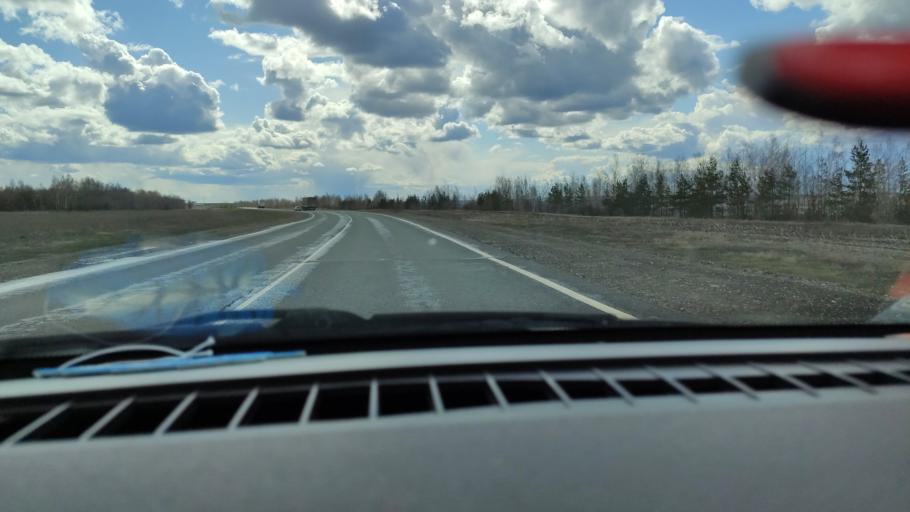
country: RU
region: Samara
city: Syzran'
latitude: 52.8589
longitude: 48.2626
